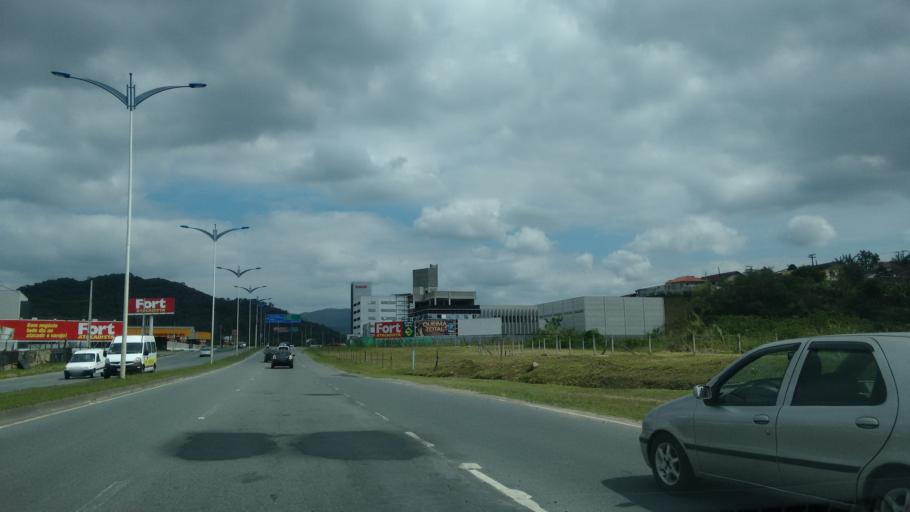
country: BR
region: Santa Catarina
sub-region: Blumenau
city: Blumenau
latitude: -26.8902
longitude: -49.0706
